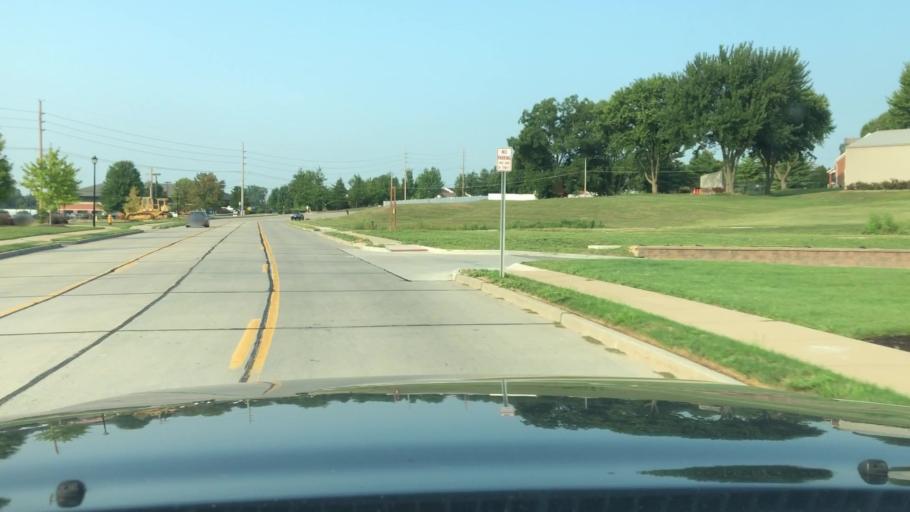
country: US
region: Missouri
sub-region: Saint Charles County
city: Saint Peters
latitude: 38.8052
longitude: -90.5550
